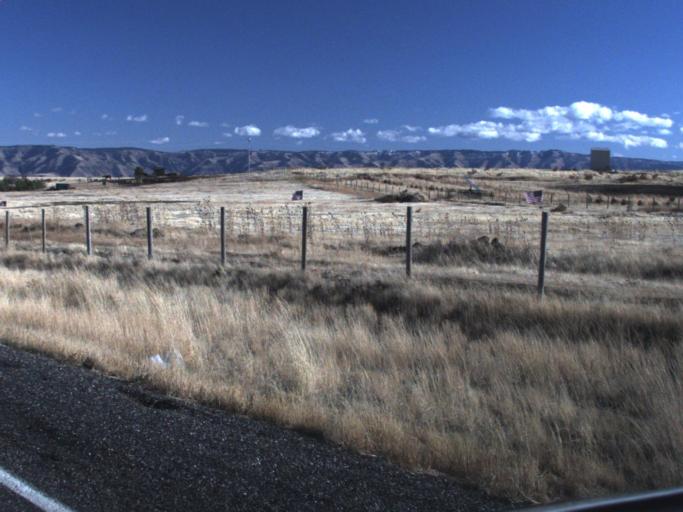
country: US
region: Washington
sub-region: Asotin County
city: Asotin
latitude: 46.1620
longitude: -117.1009
